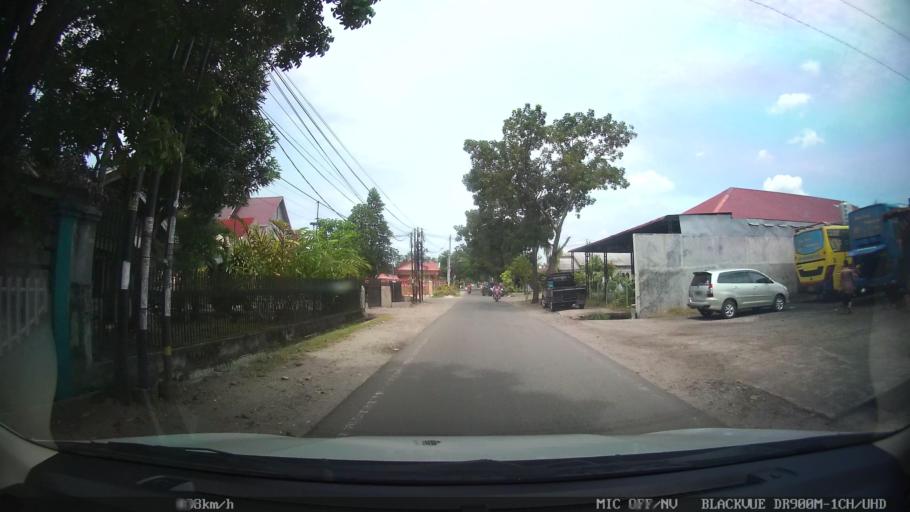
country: ID
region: North Sumatra
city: Medan
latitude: 3.5551
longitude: 98.6567
